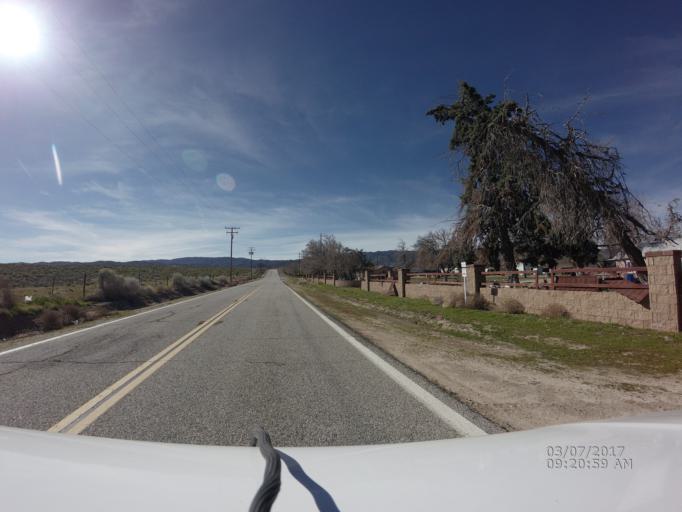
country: US
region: California
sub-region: Los Angeles County
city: Green Valley
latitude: 34.7742
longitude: -118.5899
